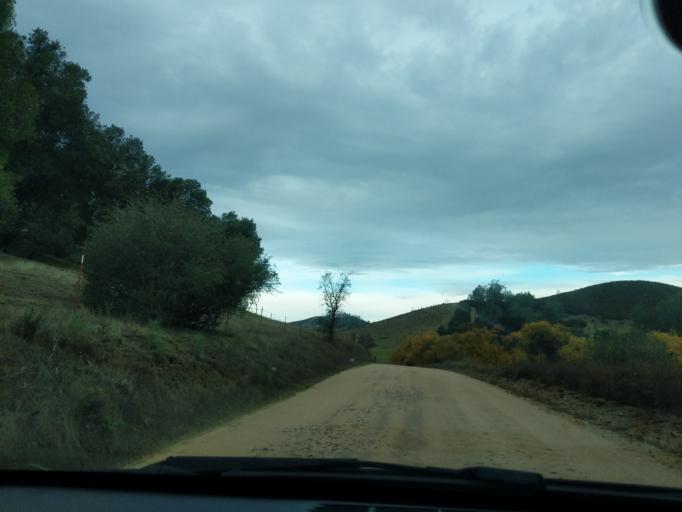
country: US
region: California
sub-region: Monterey County
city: Soledad
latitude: 36.5465
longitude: -121.2799
